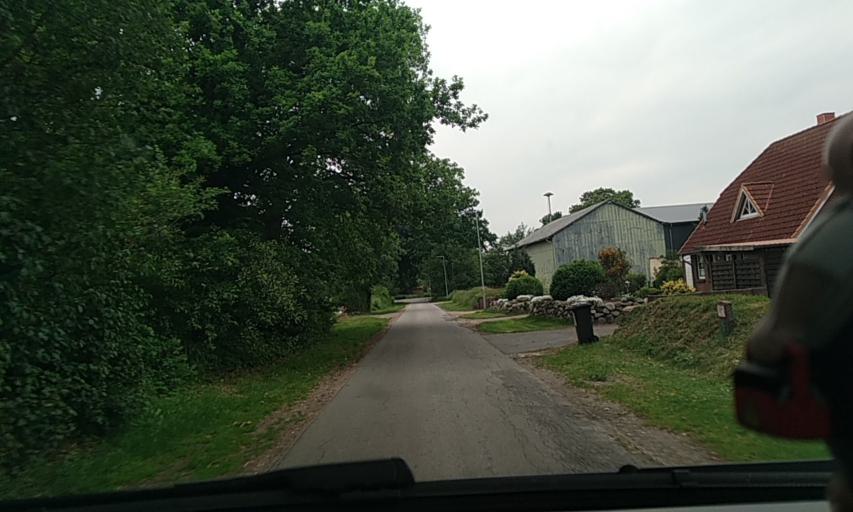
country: DE
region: Schleswig-Holstein
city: Borm
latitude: 54.3977
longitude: 9.3813
